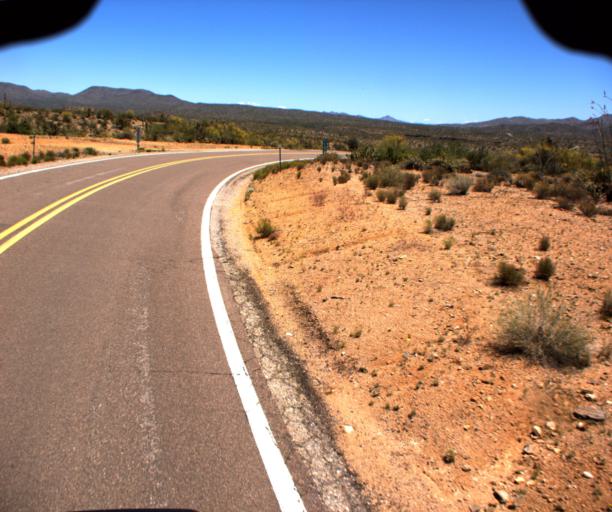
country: US
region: Arizona
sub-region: Yavapai County
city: Bagdad
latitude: 34.4600
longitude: -113.2440
